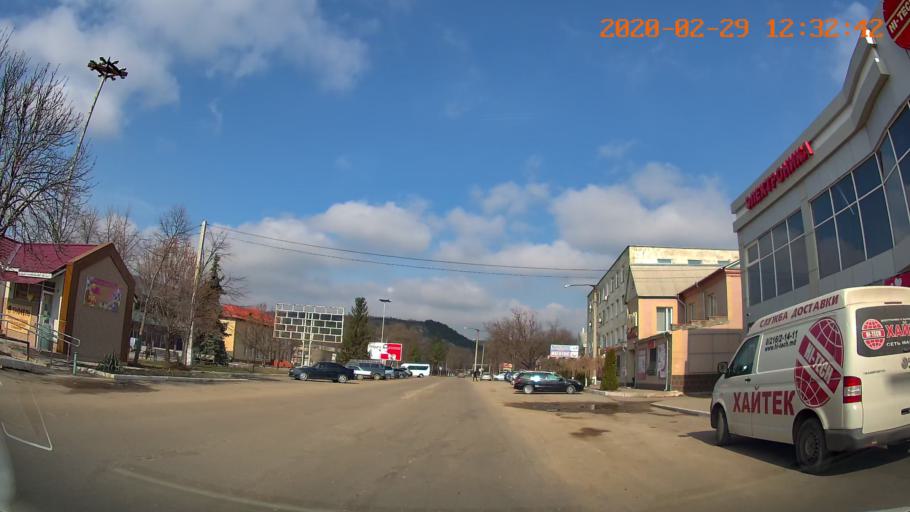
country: MD
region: Telenesti
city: Camenca
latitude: 48.0302
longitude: 28.7031
